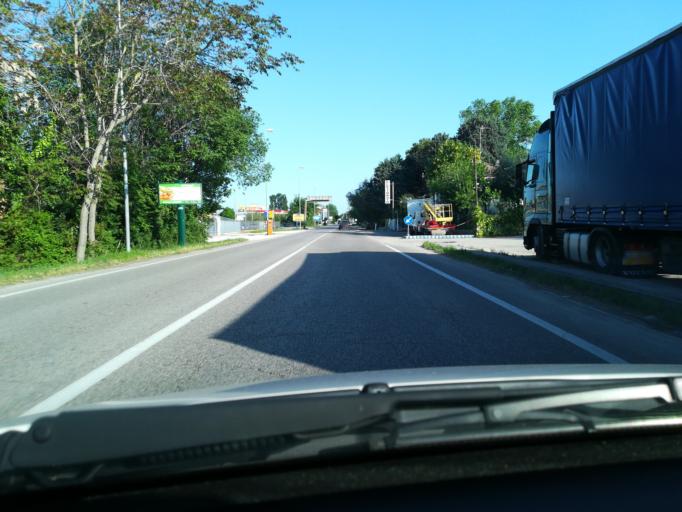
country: IT
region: Emilia-Romagna
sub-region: Provincia di Rimini
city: Misano Adriatico
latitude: 43.9829
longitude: 12.6805
